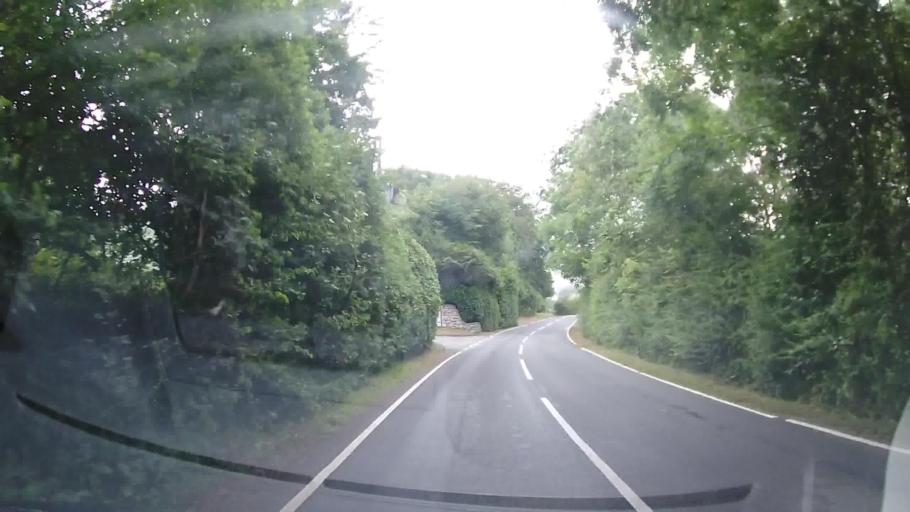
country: GB
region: Wales
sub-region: Denbighshire
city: Llandrillo
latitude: 52.9152
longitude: -3.4947
